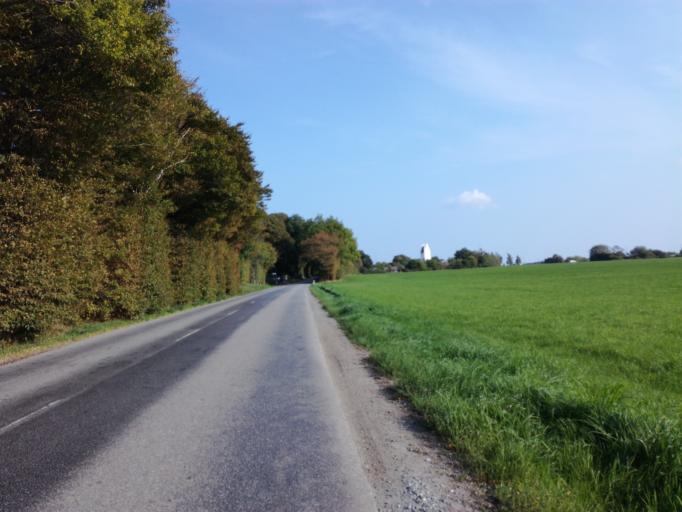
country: DK
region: South Denmark
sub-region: Vejle Kommune
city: Borkop
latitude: 55.6512
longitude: 9.6558
